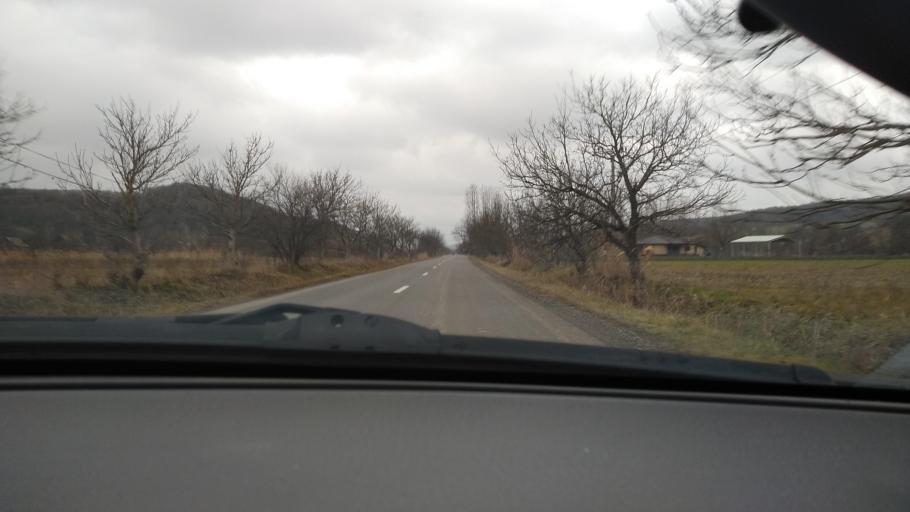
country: RO
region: Mures
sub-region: Comuna Bereni
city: Bereni
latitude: 46.5529
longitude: 24.8602
